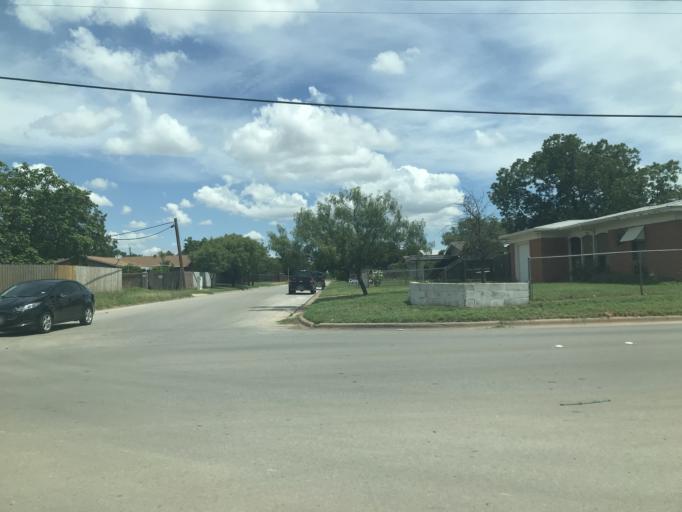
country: US
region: Texas
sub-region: Taylor County
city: Abilene
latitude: 32.4744
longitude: -99.7589
